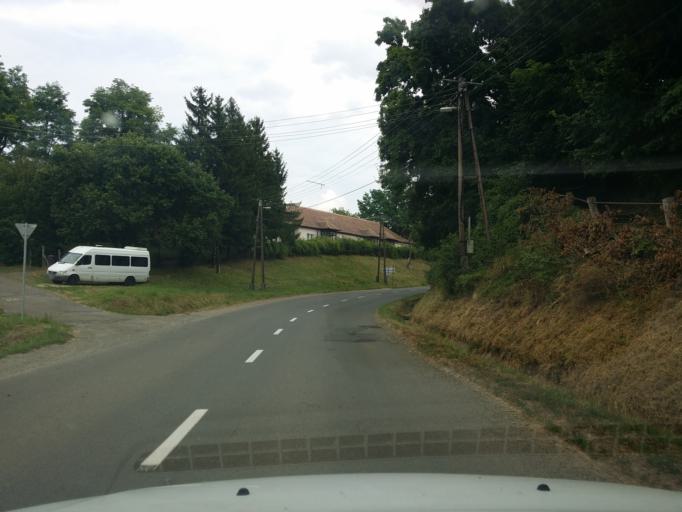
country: HU
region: Nograd
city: Romhany
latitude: 47.9662
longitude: 19.3497
